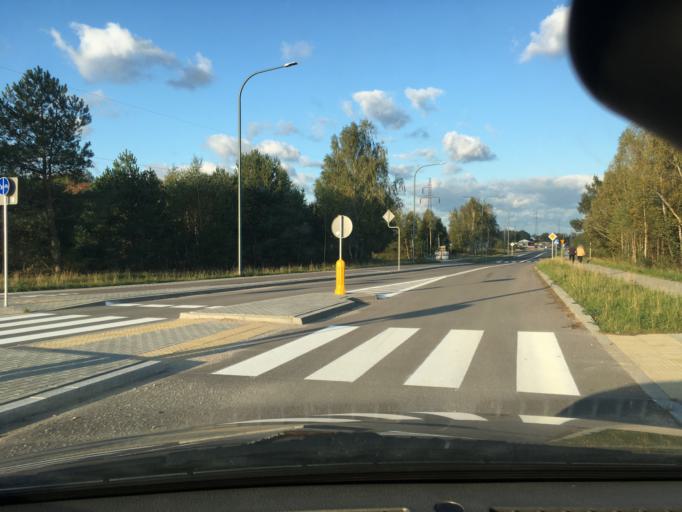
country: PL
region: Masovian Voivodeship
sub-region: Powiat piaseczynski
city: Lesznowola
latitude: 52.0452
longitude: 20.9274
